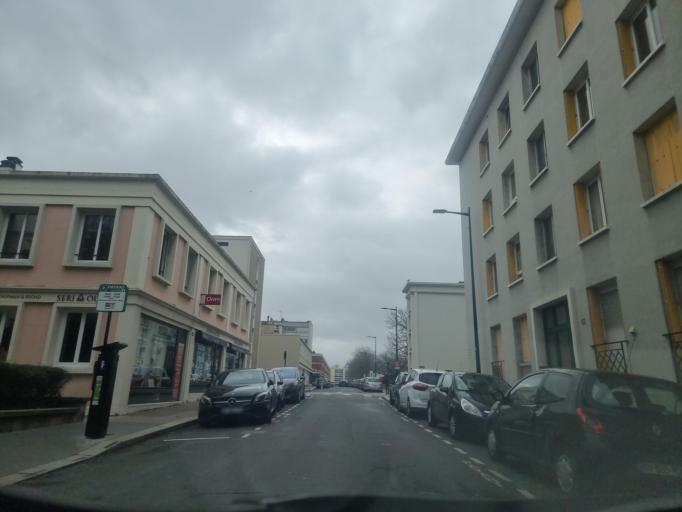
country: FR
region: Haute-Normandie
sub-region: Departement de la Seine-Maritime
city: Le Havre
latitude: 49.4928
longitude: 0.1037
